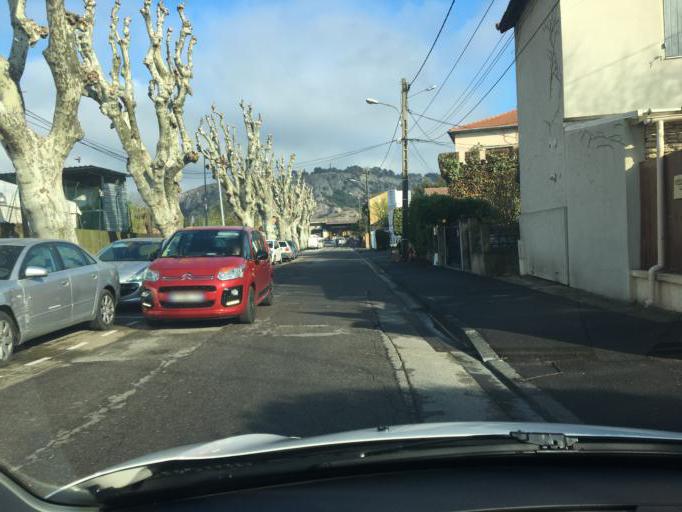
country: FR
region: Provence-Alpes-Cote d'Azur
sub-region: Departement du Vaucluse
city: Cavaillon
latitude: 43.8292
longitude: 5.0380
